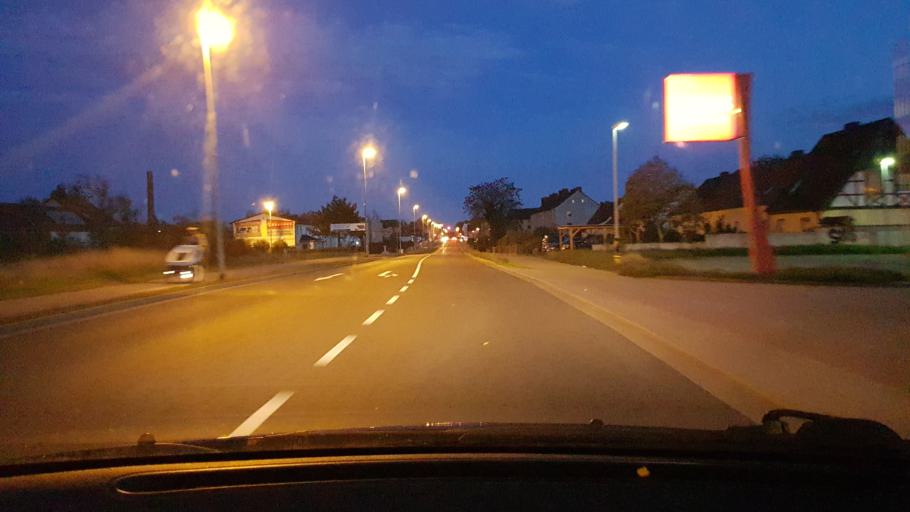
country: DE
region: Saxony-Anhalt
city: Rosslau
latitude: 51.8912
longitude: 12.2273
